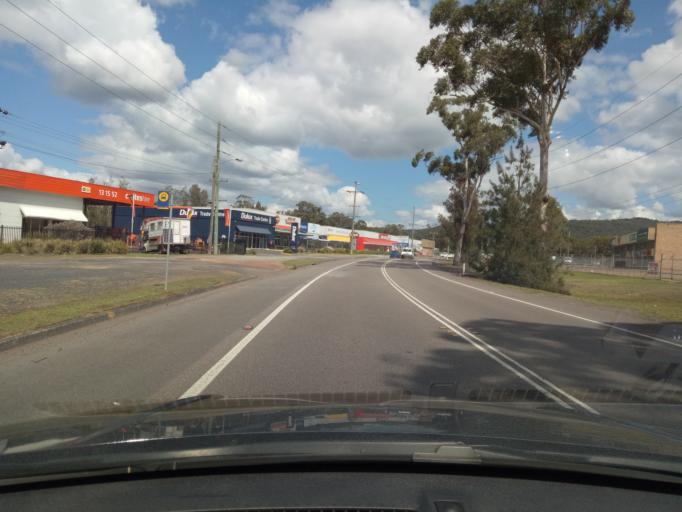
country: AU
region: New South Wales
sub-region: Gosford Shire
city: Gosford
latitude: -33.4147
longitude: 151.3323
